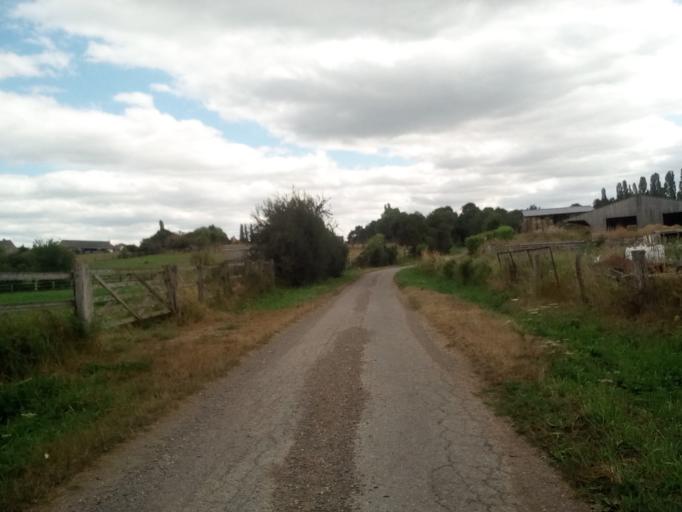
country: FR
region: Lower Normandy
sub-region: Departement du Calvados
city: Troarn
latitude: 49.1714
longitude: -0.1429
